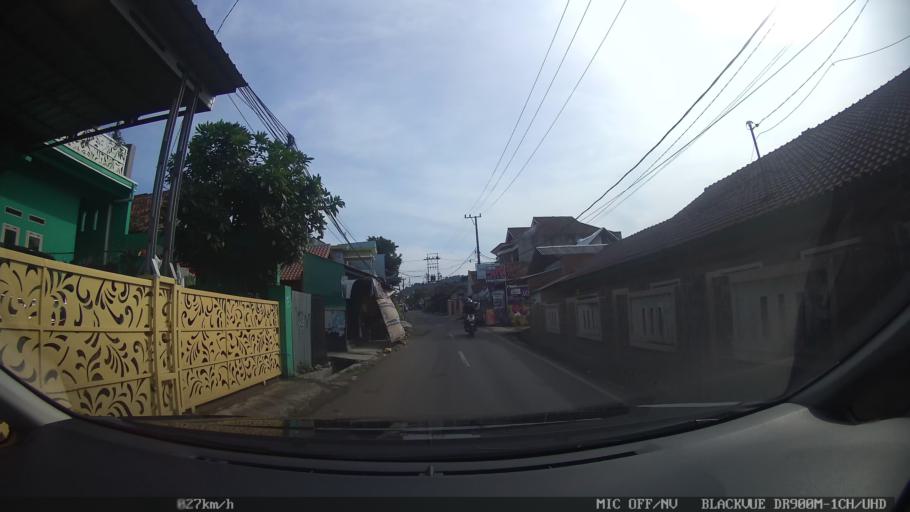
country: ID
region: Lampung
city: Kedaton
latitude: -5.3996
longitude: 105.2642
